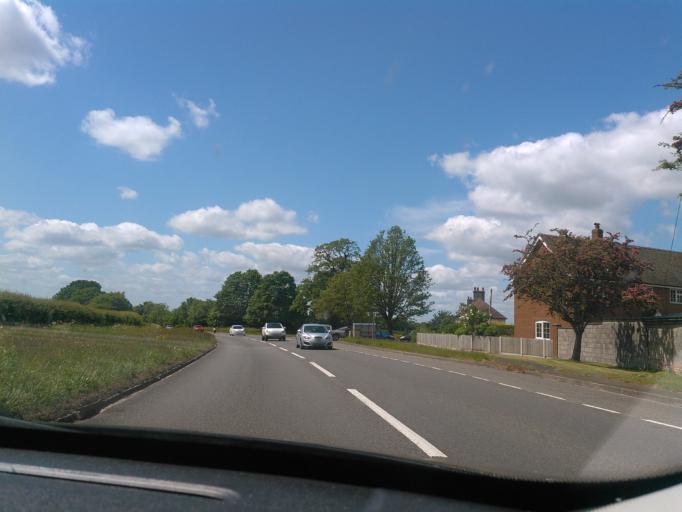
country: GB
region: England
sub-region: Shropshire
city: Market Drayton
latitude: 52.9139
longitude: -2.4436
